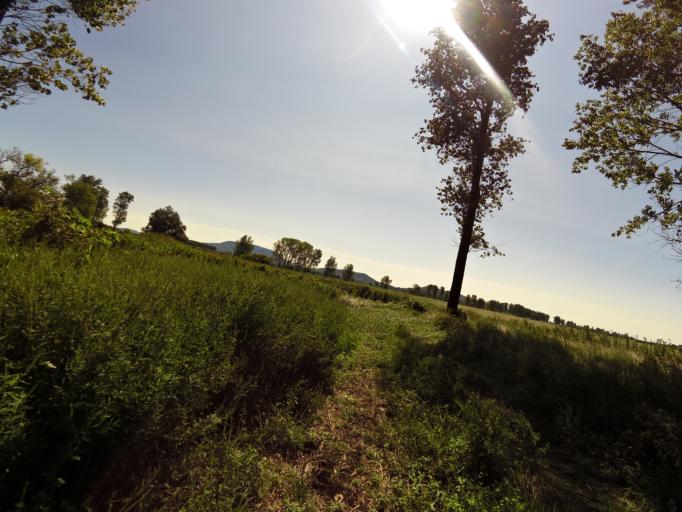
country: HU
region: Veszprem
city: Tapolca
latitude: 46.8323
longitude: 17.4130
